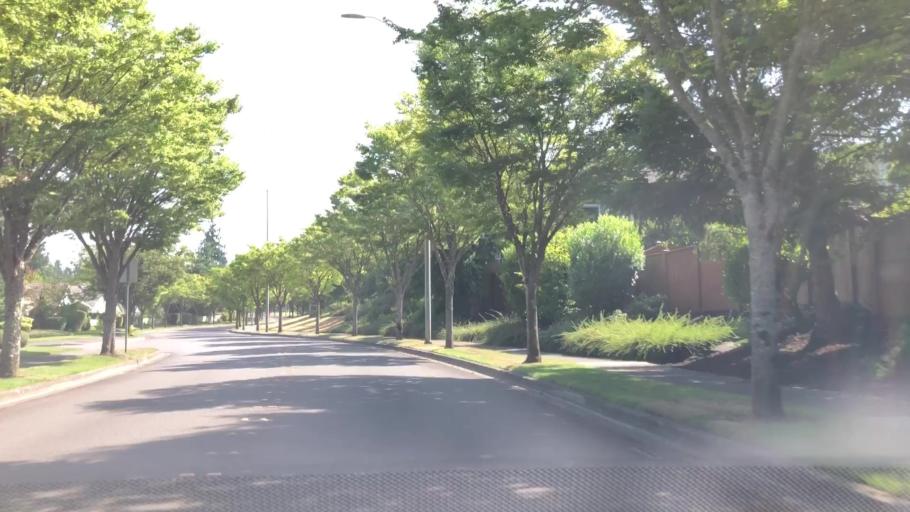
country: US
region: Washington
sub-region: Thurston County
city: Tanglewilde-Thompson Place
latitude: 47.0938
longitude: -122.7594
